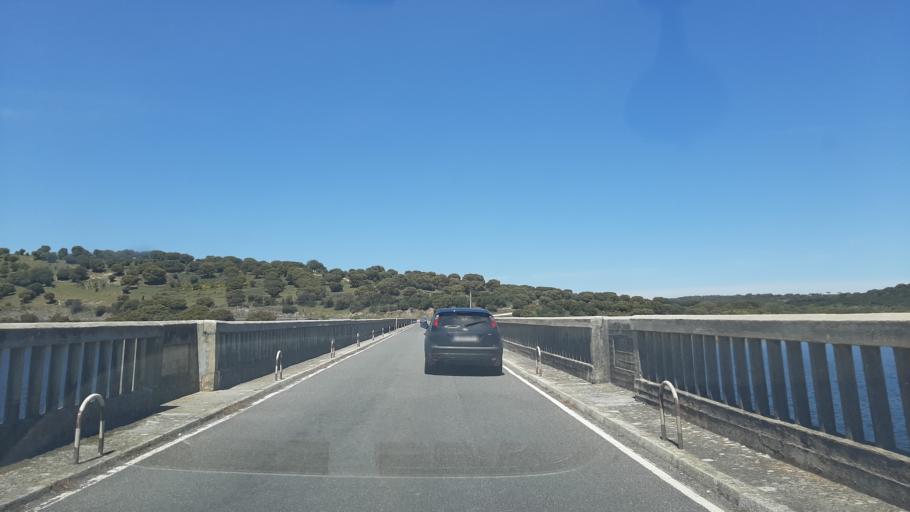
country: ES
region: Castille and Leon
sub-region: Provincia de Salamanca
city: Guijo de Avila
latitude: 40.5525
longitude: -5.6286
